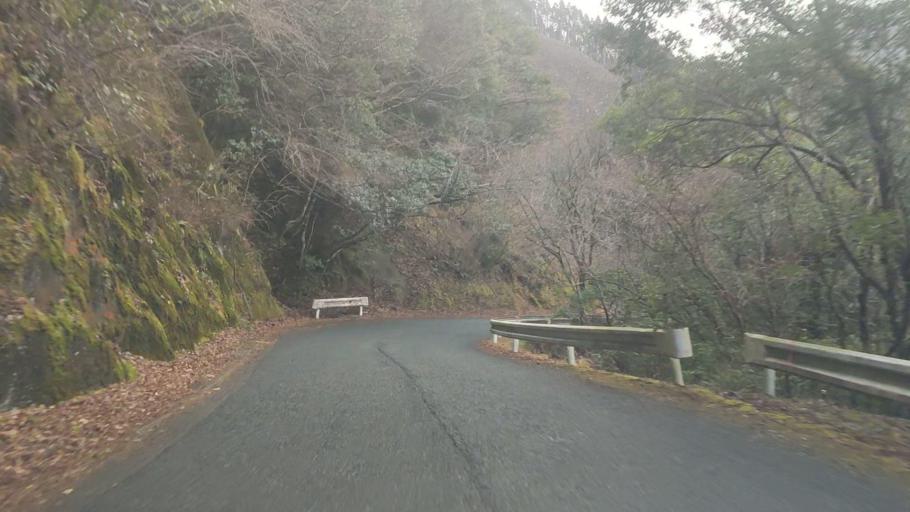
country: JP
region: Kumamoto
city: Matsubase
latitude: 32.4865
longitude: 130.8986
